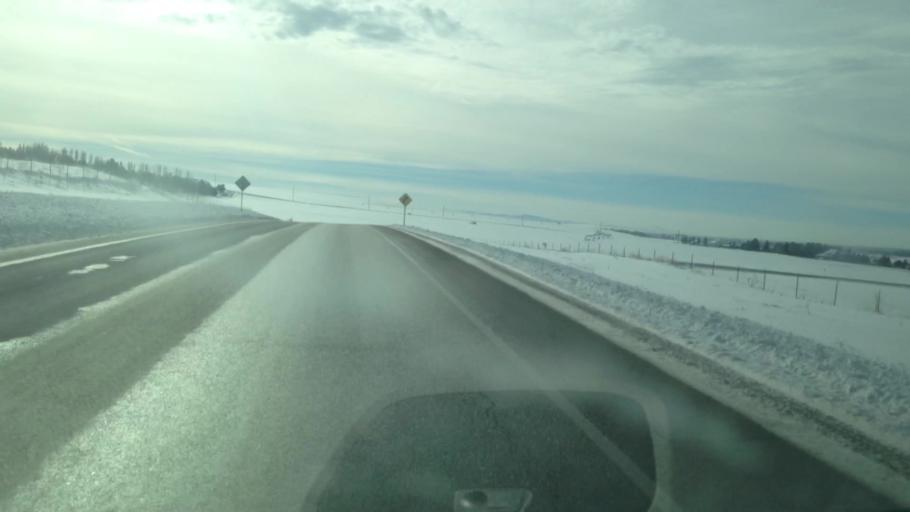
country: US
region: Idaho
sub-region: Madison County
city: Rexburg
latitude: 43.8073
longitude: -111.7895
